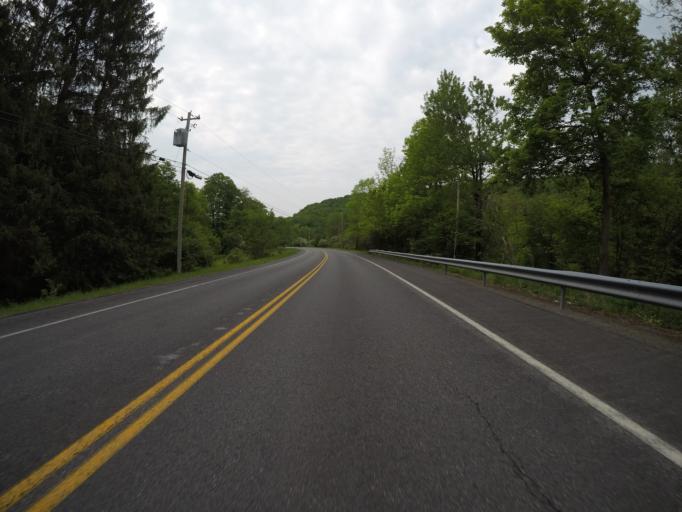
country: US
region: New York
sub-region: Sullivan County
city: Livingston Manor
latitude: 41.9860
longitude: -74.8946
